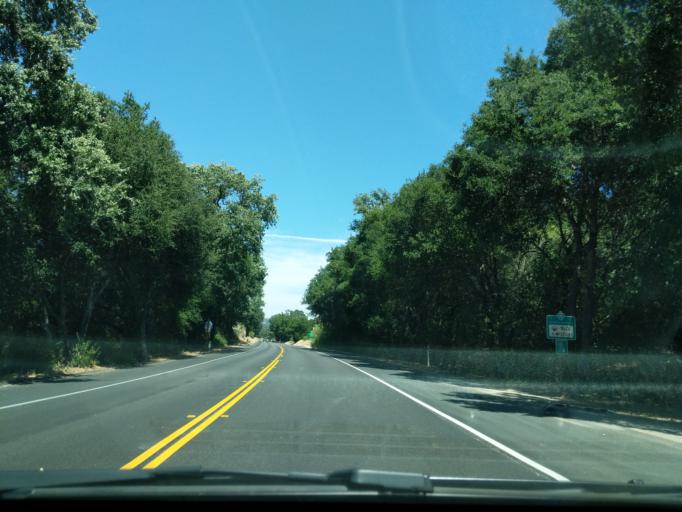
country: US
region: California
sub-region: San Luis Obispo County
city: Santa Margarita
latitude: 35.3836
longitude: -120.6265
